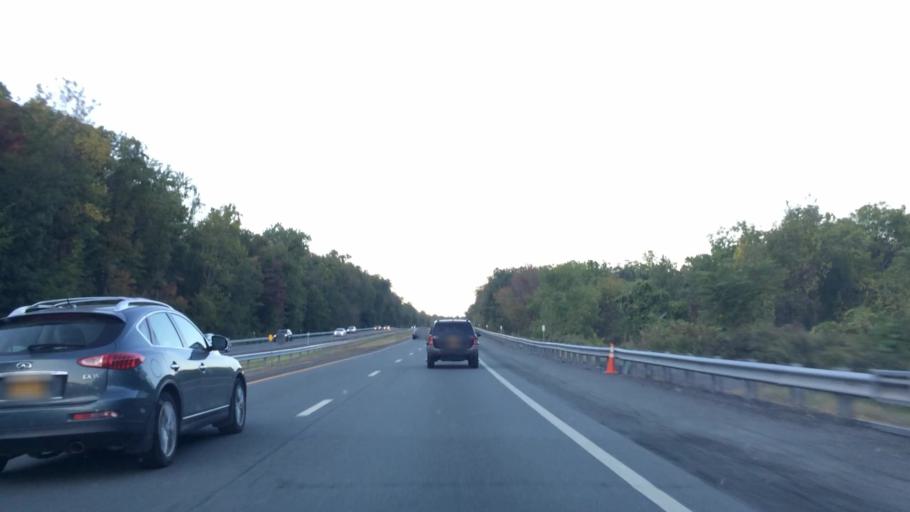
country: US
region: New York
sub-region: Orange County
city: Woodbury
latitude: 41.3832
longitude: -74.1013
